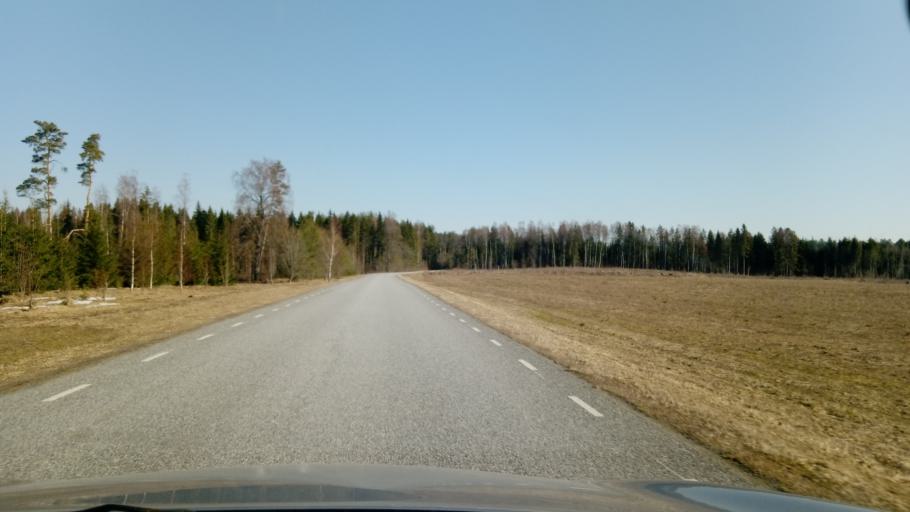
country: EE
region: Laeaene-Virumaa
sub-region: Tamsalu vald
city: Tamsalu
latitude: 59.2262
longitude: 26.1646
